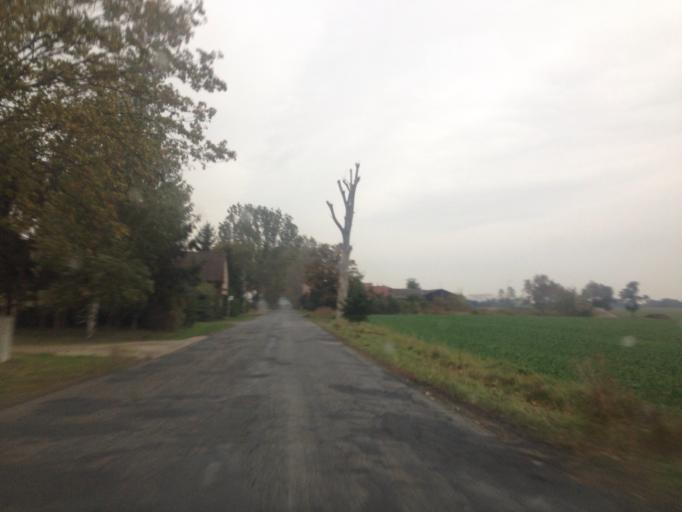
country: PL
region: Greater Poland Voivodeship
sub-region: Powiat poznanski
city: Kleszczewo
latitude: 52.3484
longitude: 17.1519
